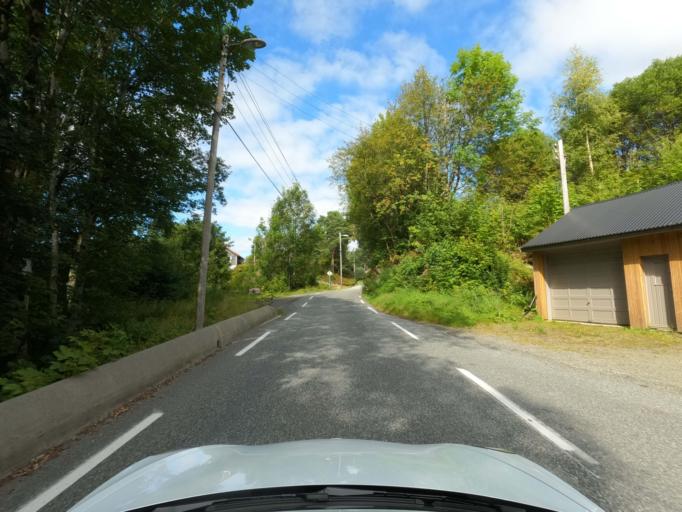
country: NO
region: Hordaland
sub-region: Bergen
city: Sandsli
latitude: 60.2702
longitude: 5.3515
